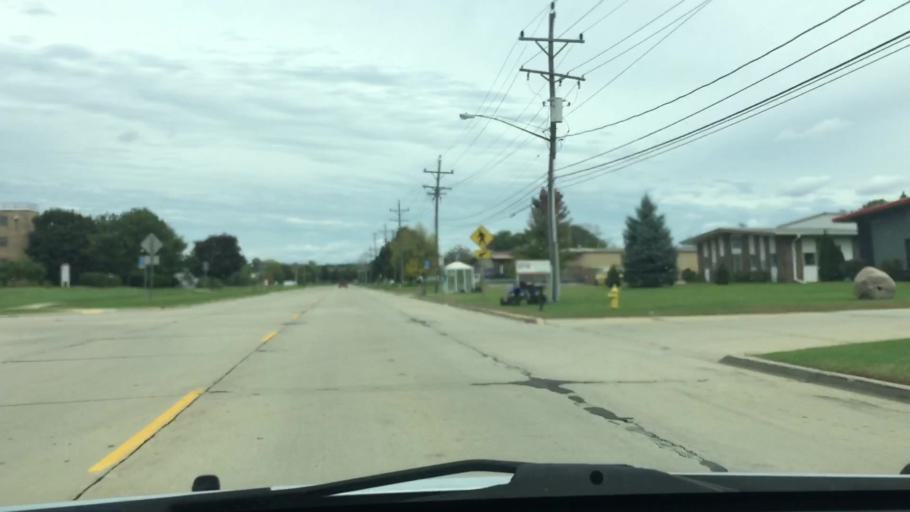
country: US
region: Wisconsin
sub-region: Waukesha County
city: Waukesha
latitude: 42.9892
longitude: -88.2496
